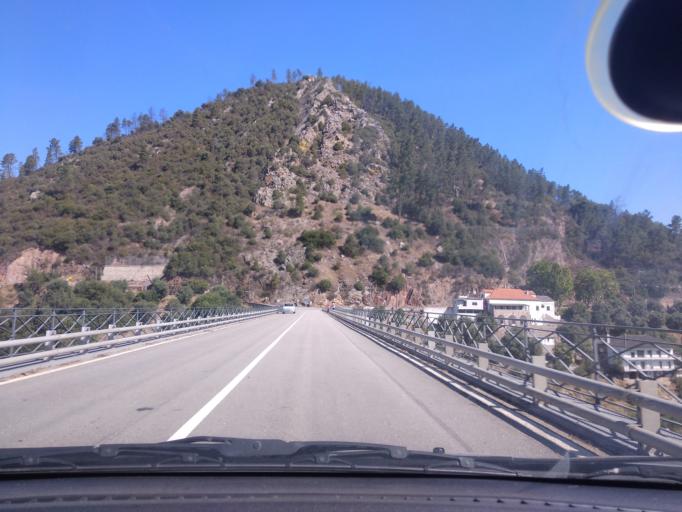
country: PT
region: Portalegre
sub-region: Nisa
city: Nisa
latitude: 39.6466
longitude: -7.6762
